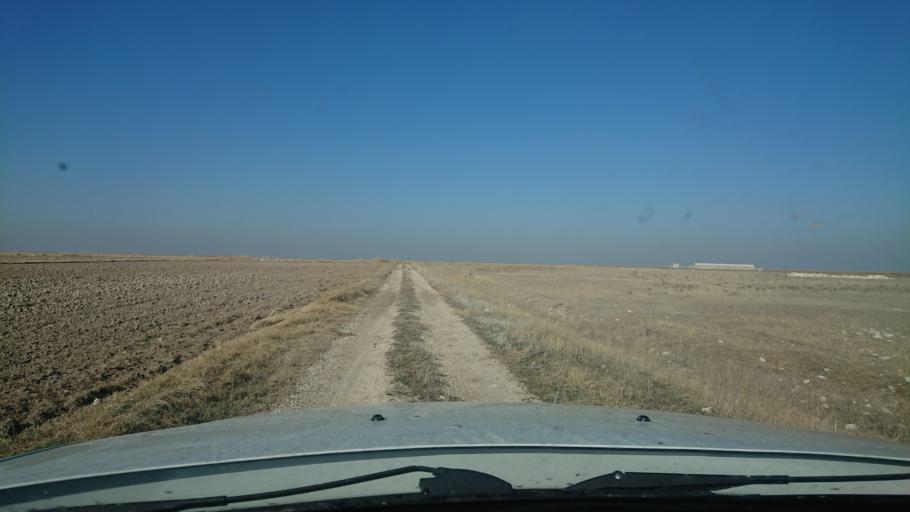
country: TR
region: Aksaray
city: Sultanhani
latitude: 38.3164
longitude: 33.5268
